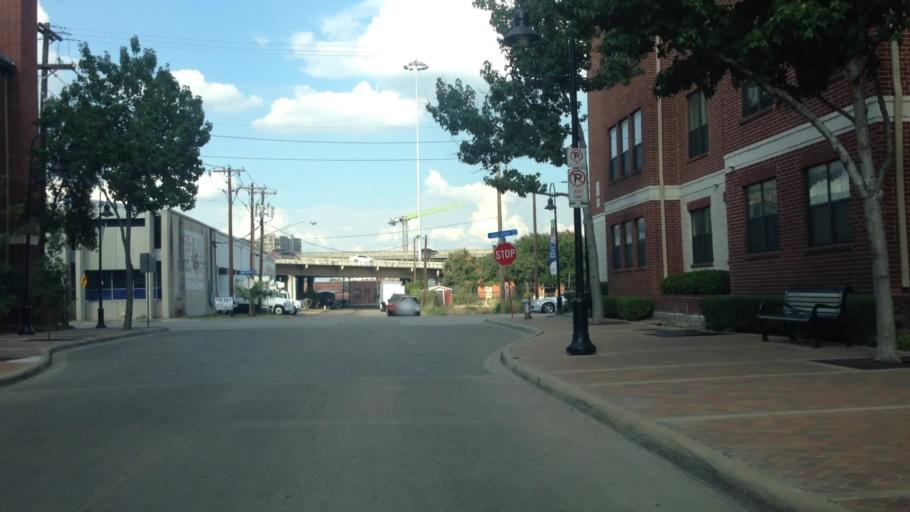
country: US
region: Texas
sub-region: Dallas County
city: Dallas
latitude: 32.7798
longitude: -96.7859
